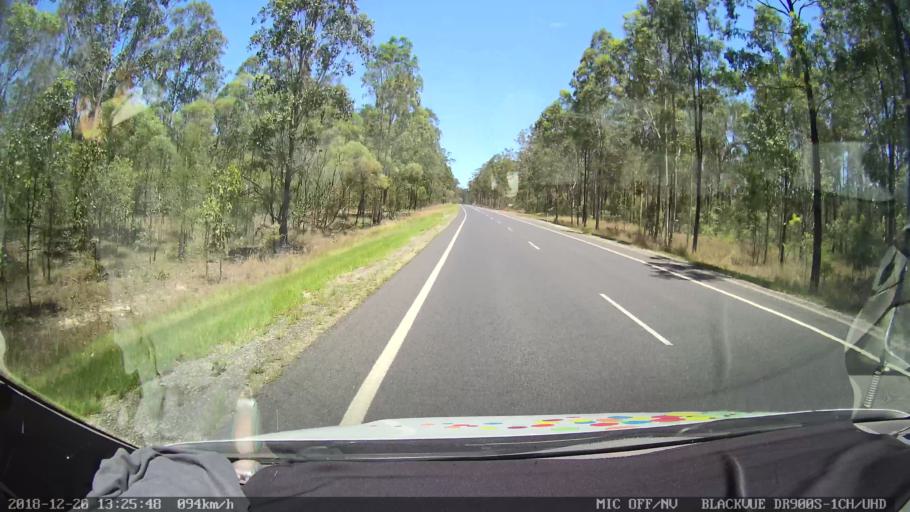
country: AU
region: New South Wales
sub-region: Richmond Valley
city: Casino
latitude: -29.1363
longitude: 152.9959
